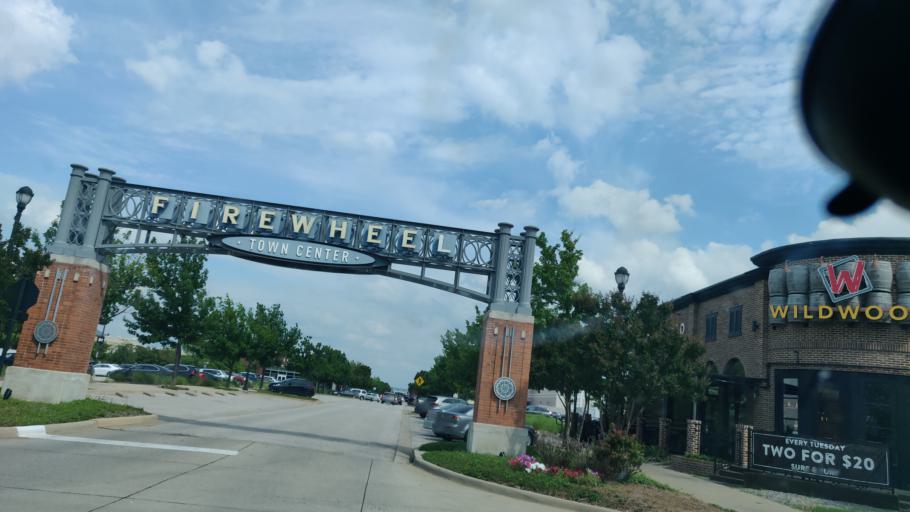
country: US
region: Texas
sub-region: Dallas County
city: Sachse
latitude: 32.9534
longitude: -96.6150
